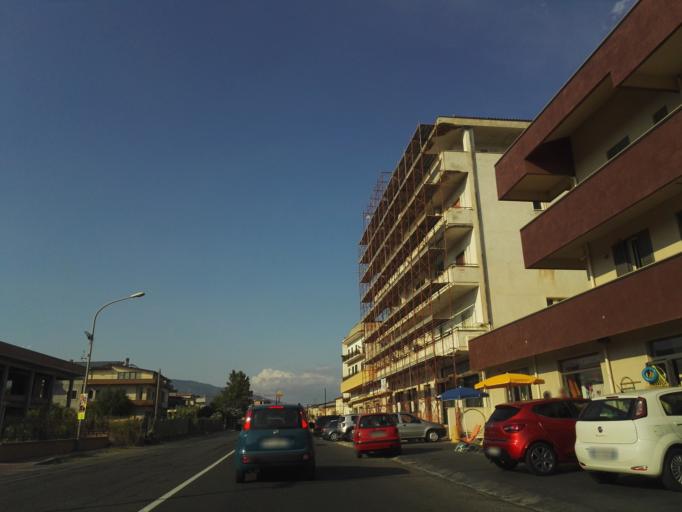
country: IT
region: Calabria
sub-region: Provincia di Reggio Calabria
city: Siderno
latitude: 38.2843
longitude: 16.3131
